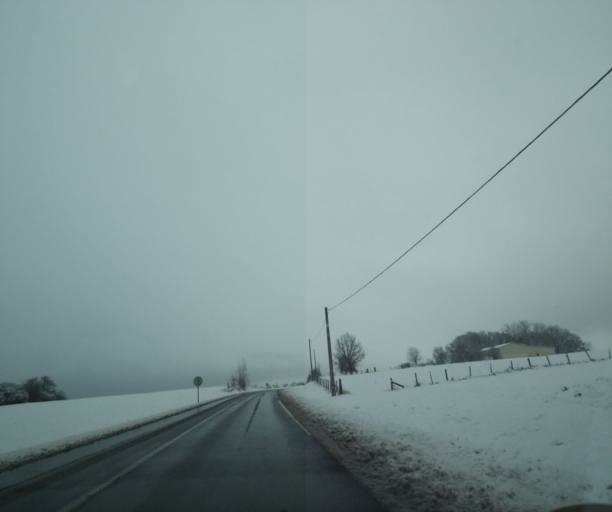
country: FR
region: Champagne-Ardenne
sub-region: Departement de la Haute-Marne
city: Montier-en-Der
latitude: 48.5297
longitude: 4.8158
